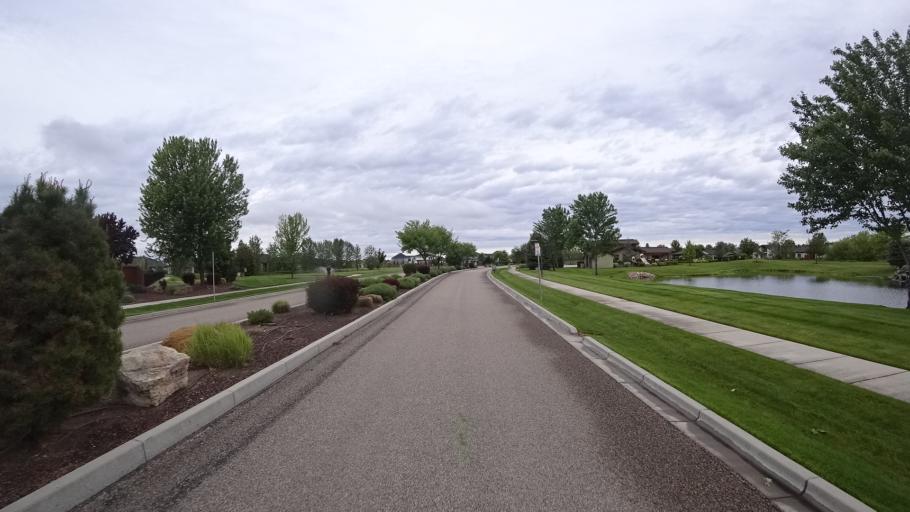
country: US
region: Idaho
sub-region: Ada County
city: Star
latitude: 43.6883
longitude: -116.4747
